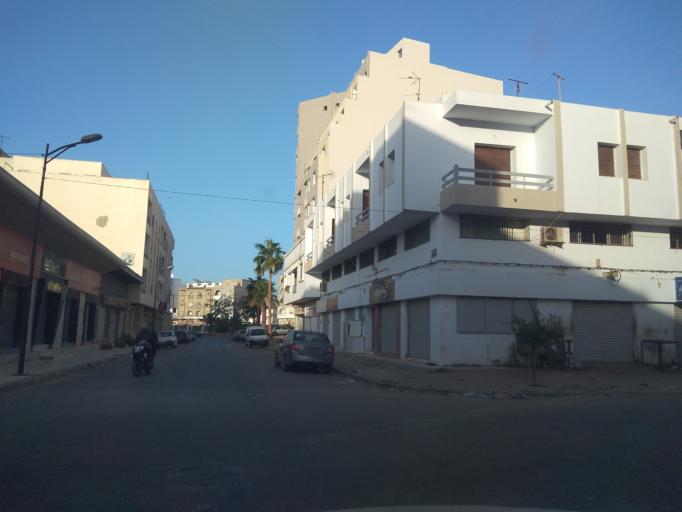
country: TN
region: Safaqis
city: Sfax
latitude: 34.7449
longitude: 10.7638
